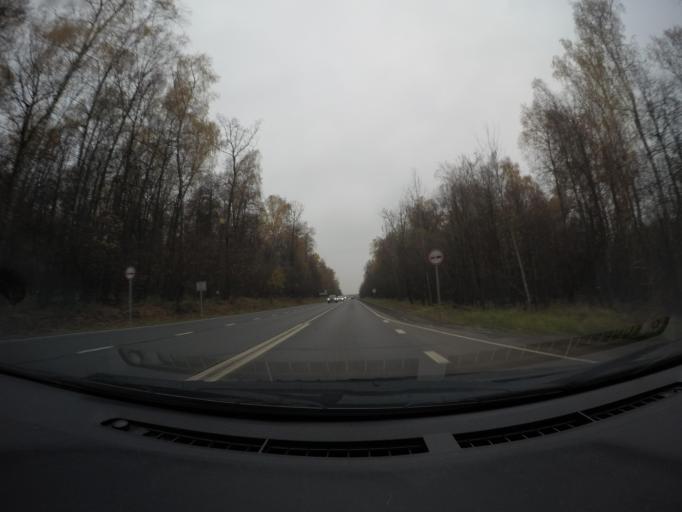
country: RU
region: Moskovskaya
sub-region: Podol'skiy Rayon
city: Podol'sk
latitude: 55.3824
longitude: 37.6305
